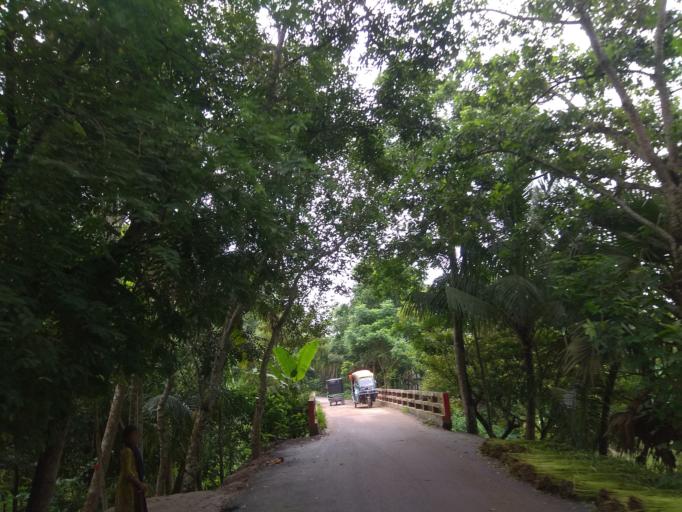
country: BD
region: Dhaka
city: Dohar
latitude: 23.4461
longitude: 90.0629
